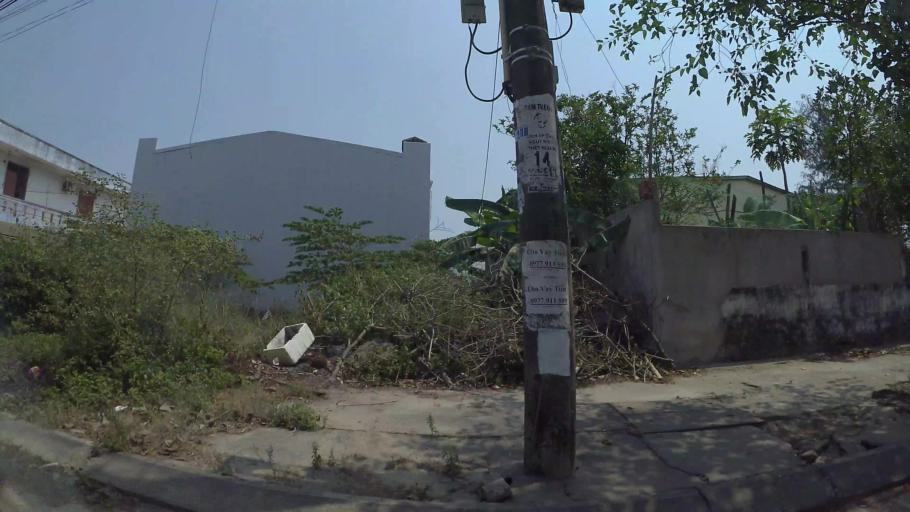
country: VN
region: Da Nang
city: Ngu Hanh Son
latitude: 16.0097
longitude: 108.2526
